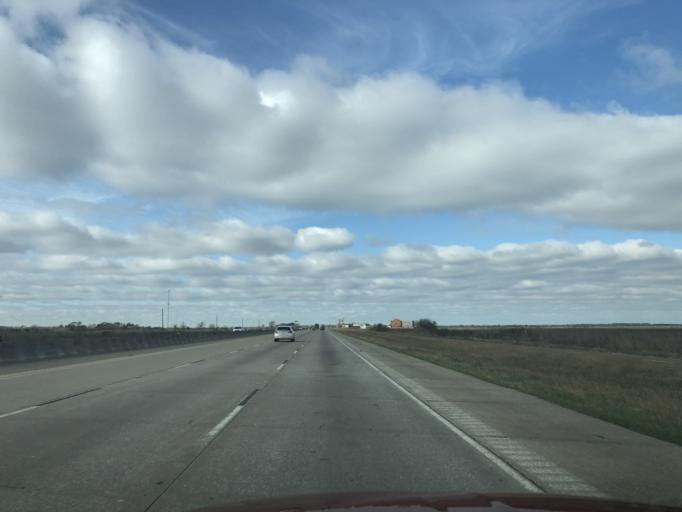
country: US
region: Texas
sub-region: Chambers County
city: Winnie
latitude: 29.8331
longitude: -94.5268
